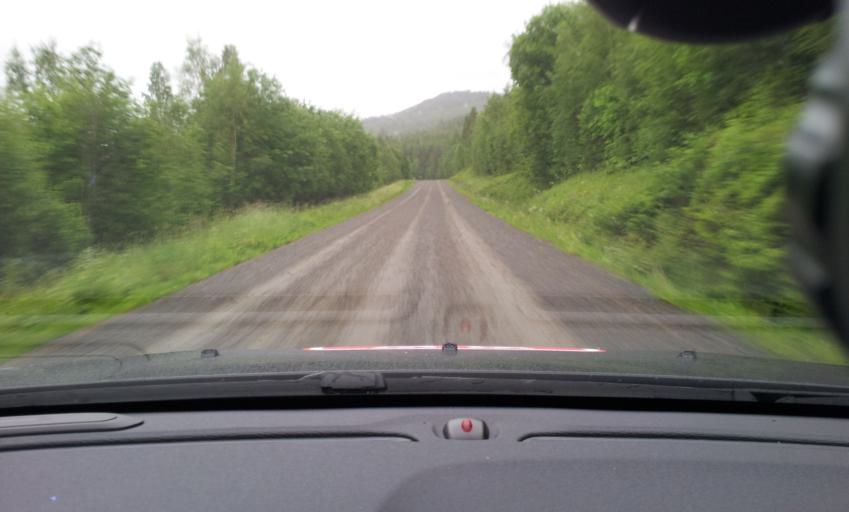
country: SE
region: Jaemtland
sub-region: Ragunda Kommun
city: Hammarstrand
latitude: 63.1352
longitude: 16.1111
